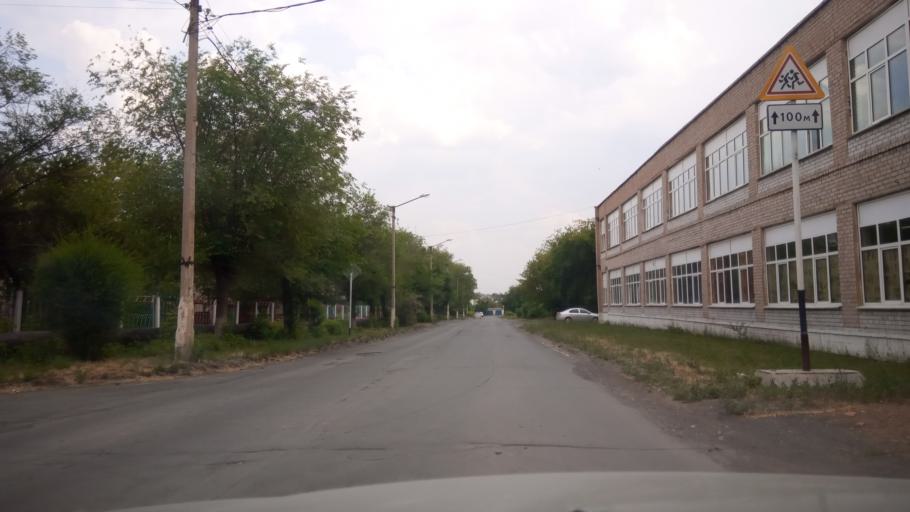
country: RU
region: Orenburg
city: Novotroitsk
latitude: 51.2032
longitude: 58.3069
